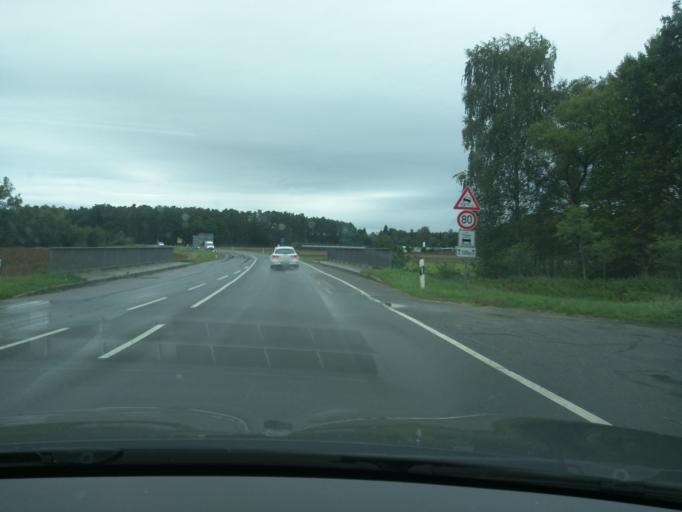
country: DE
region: Bavaria
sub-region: Upper Palatinate
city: Schwandorf in Bayern
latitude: 49.3474
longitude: 12.1439
